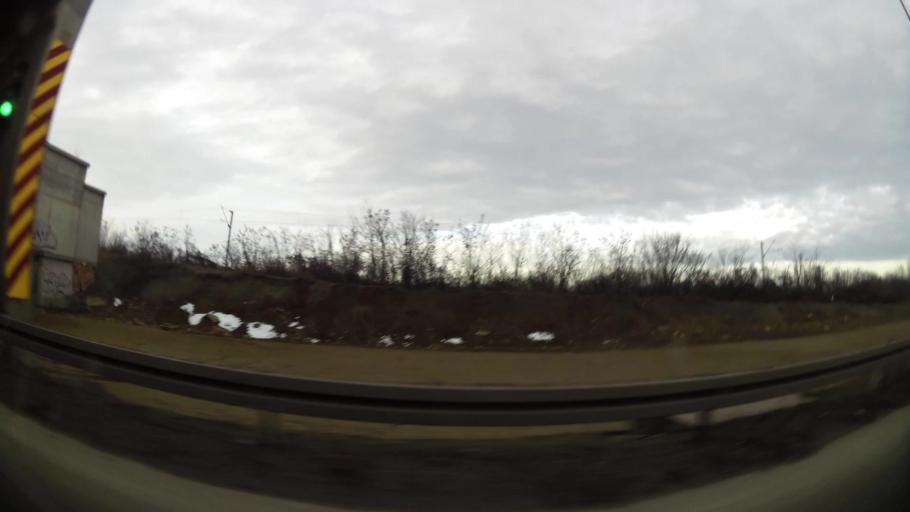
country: RS
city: Ostruznica
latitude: 44.7275
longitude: 20.3514
